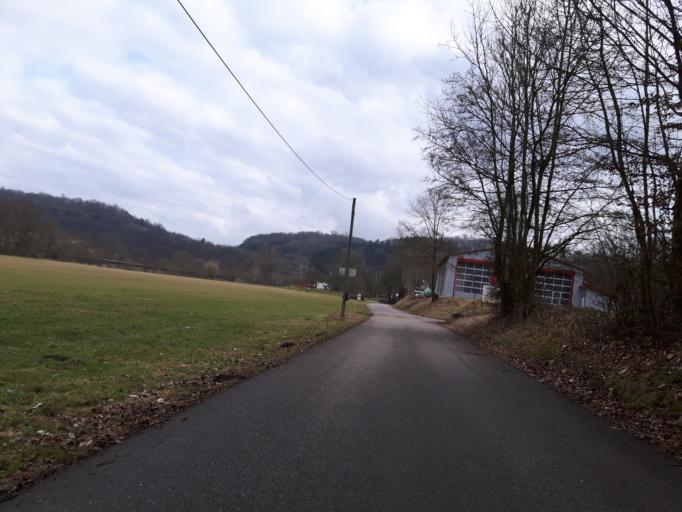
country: DE
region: Baden-Wuerttemberg
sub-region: Regierungsbezirk Stuttgart
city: Jagsthausen
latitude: 49.2515
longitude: 9.4513
